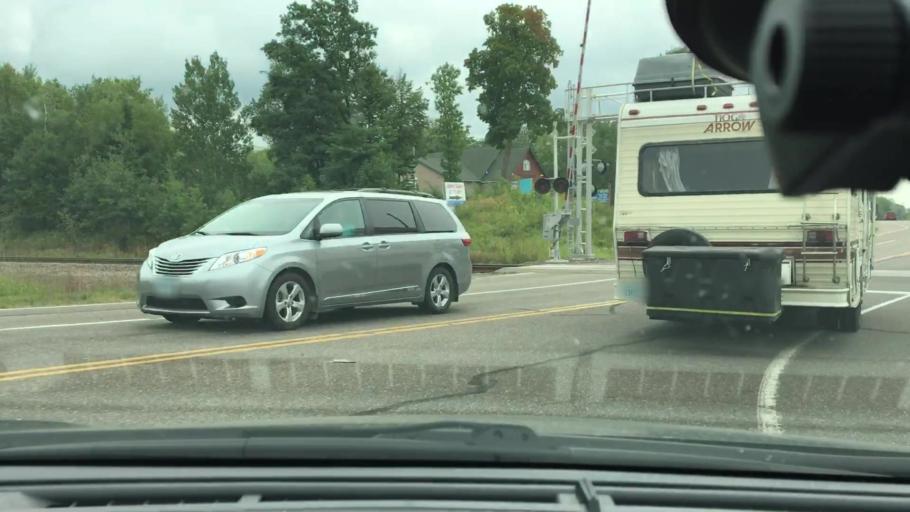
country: US
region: Minnesota
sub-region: Crow Wing County
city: Crosby
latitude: 46.4752
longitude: -93.8927
